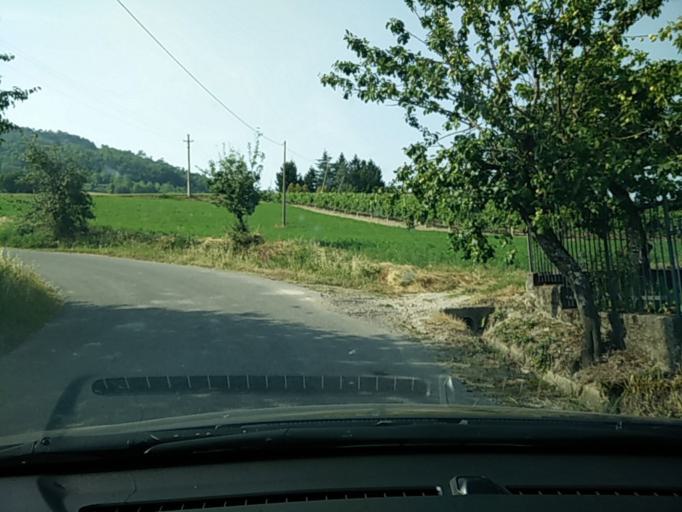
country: IT
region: Lombardy
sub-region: Provincia di Pavia
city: Susella
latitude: 44.9077
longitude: 9.0998
